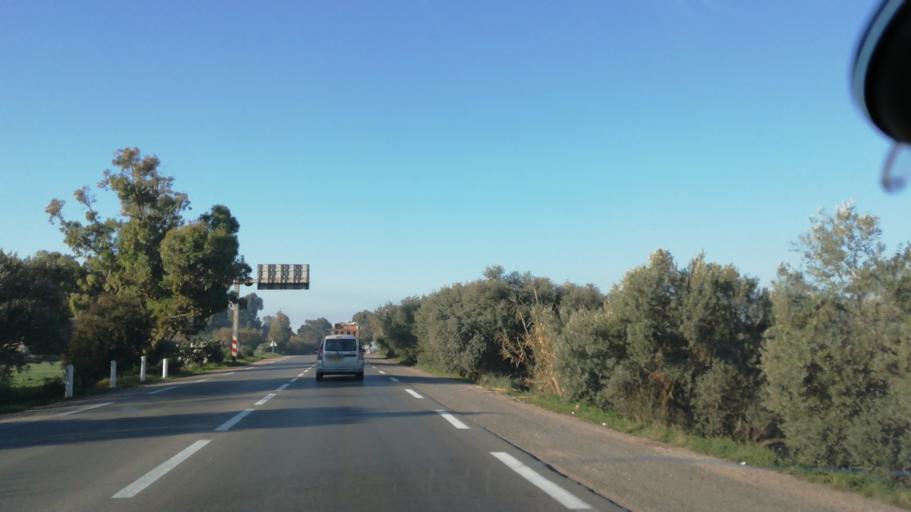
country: DZ
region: Tlemcen
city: Remchi
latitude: 35.0835
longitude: -1.4394
